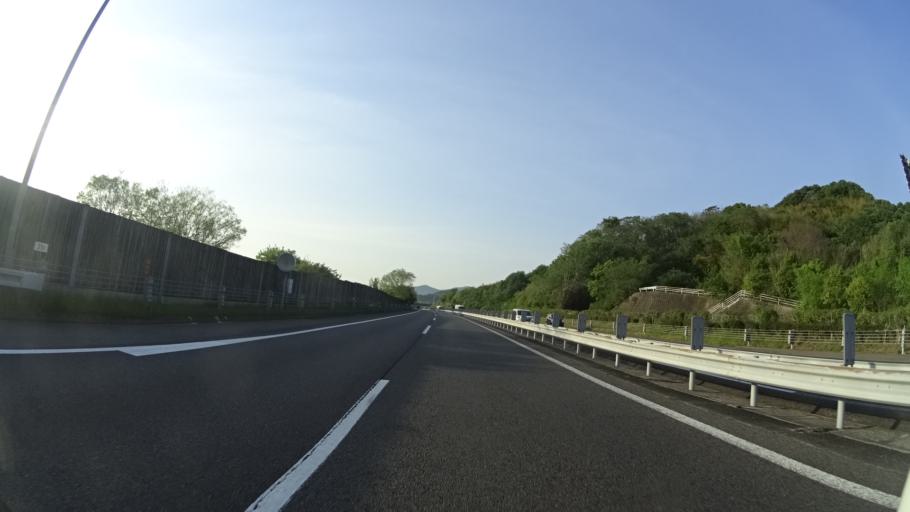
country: JP
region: Kagawa
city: Tadotsu
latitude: 34.1841
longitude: 133.7342
